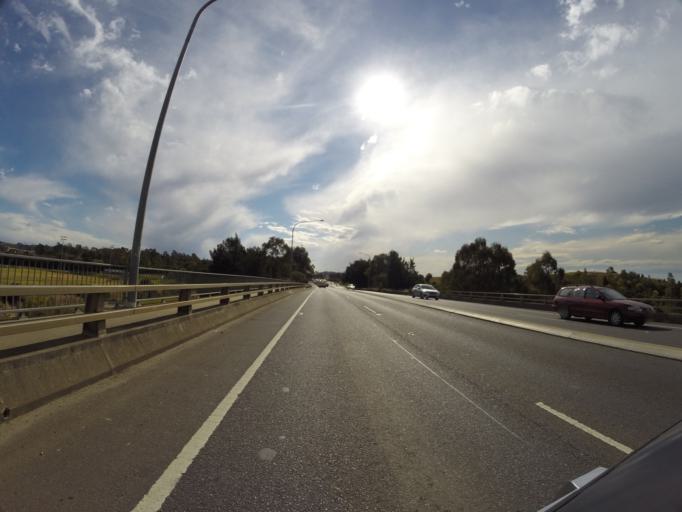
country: AU
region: New South Wales
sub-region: Campbelltown Municipality
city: Campbelltown
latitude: -34.0703
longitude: 150.8042
